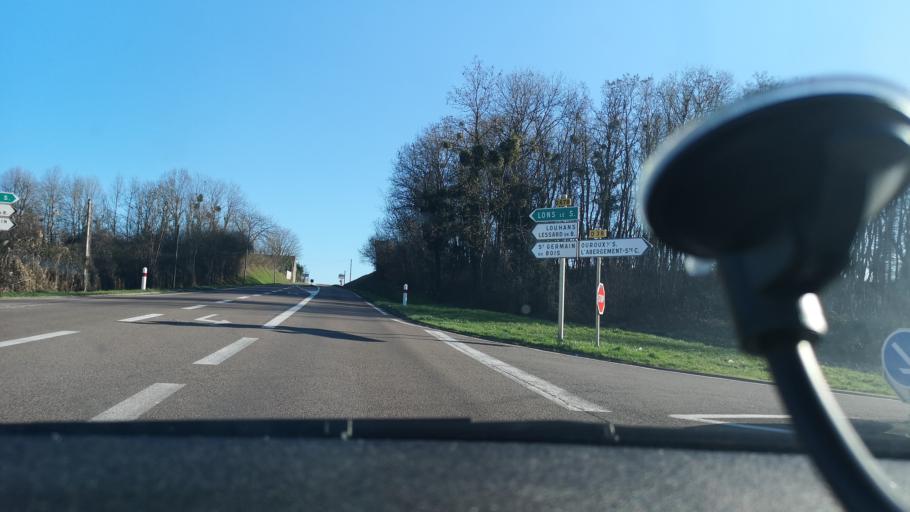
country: FR
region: Bourgogne
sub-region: Departement de Saone-et-Loire
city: Saint-Germain-du-Plain
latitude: 46.7564
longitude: 5.0083
